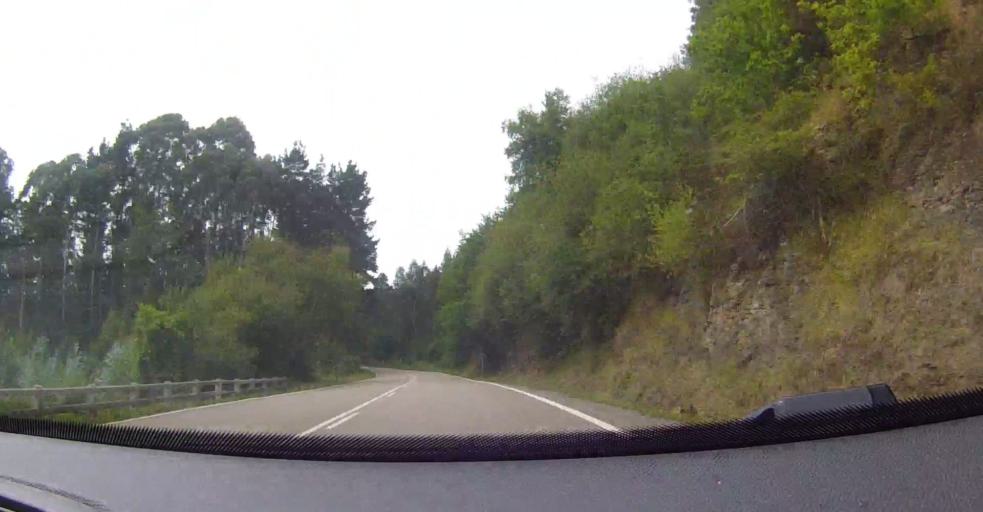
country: ES
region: Basque Country
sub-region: Bizkaia
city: Balmaseda
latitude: 43.2462
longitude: -3.2817
